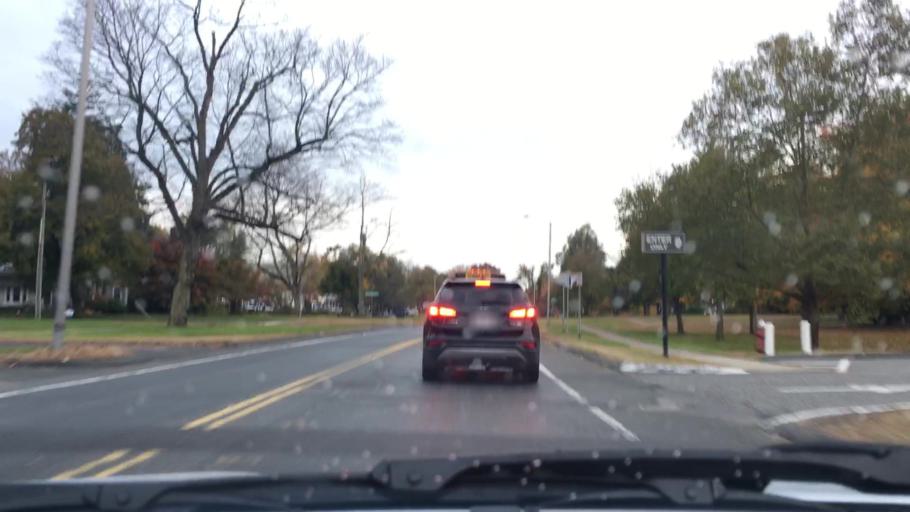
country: US
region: Massachusetts
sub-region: Hampden County
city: Longmeadow
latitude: 42.0598
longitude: -72.5799
